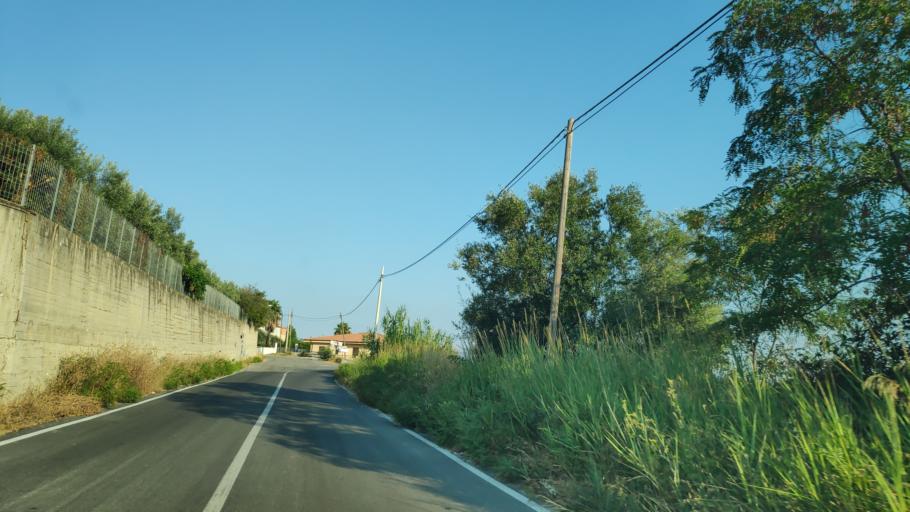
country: IT
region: Calabria
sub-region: Provincia di Reggio Calabria
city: Caulonia Marina
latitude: 38.3639
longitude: 16.4584
